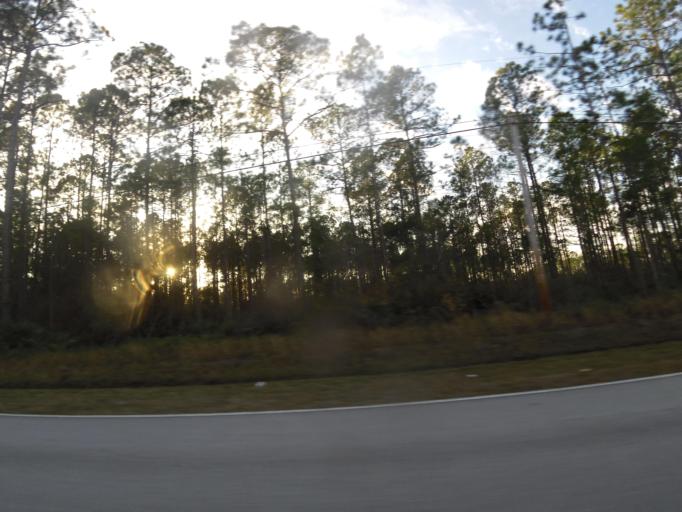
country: US
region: Florida
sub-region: Duval County
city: Baldwin
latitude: 30.1880
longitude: -81.9910
